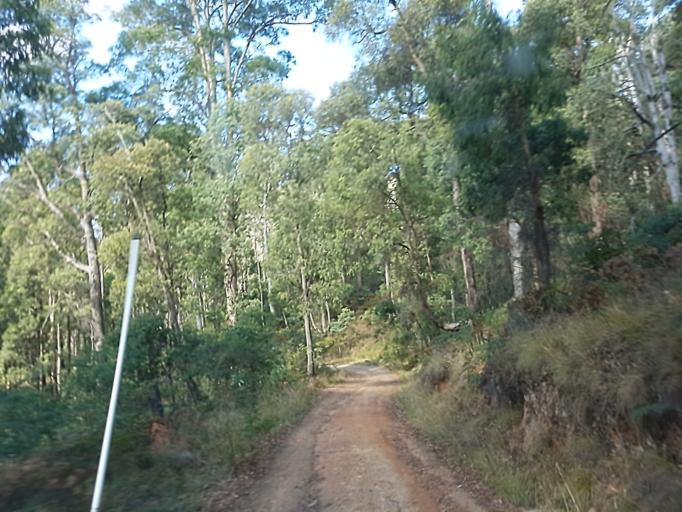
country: AU
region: Victoria
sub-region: Alpine
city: Mount Beauty
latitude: -36.9161
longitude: 147.0448
